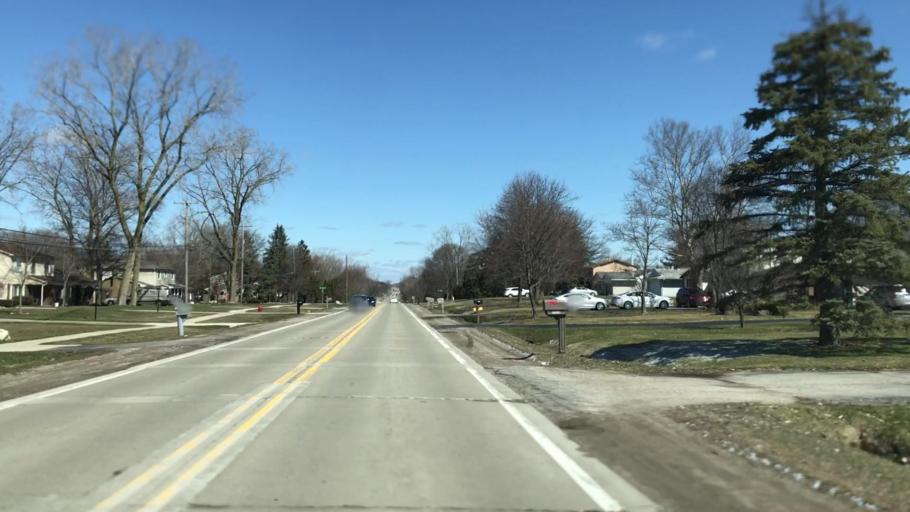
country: US
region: Michigan
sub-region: Oakland County
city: Novi
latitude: 42.4548
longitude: -83.4546
